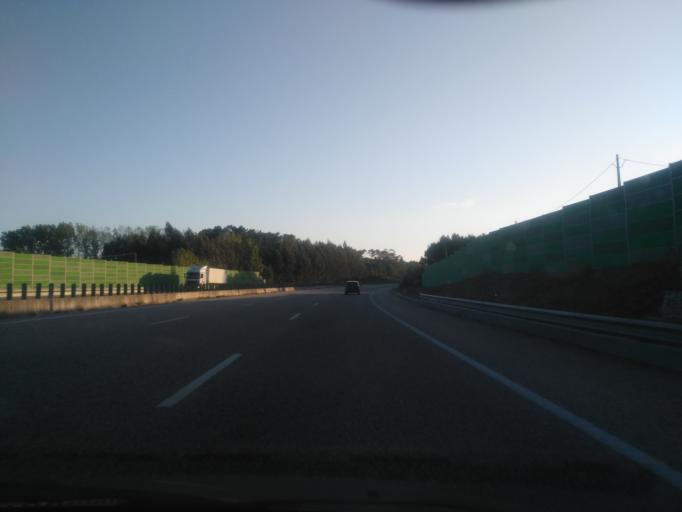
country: PT
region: Leiria
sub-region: Leiria
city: Monte Redondo
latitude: 39.9262
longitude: -8.7832
